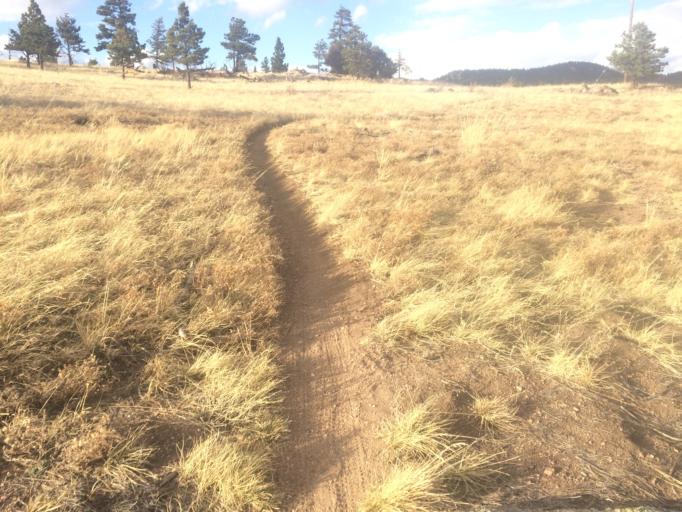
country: US
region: Colorado
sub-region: Boulder County
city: Coal Creek
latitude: 39.9514
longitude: -105.3378
